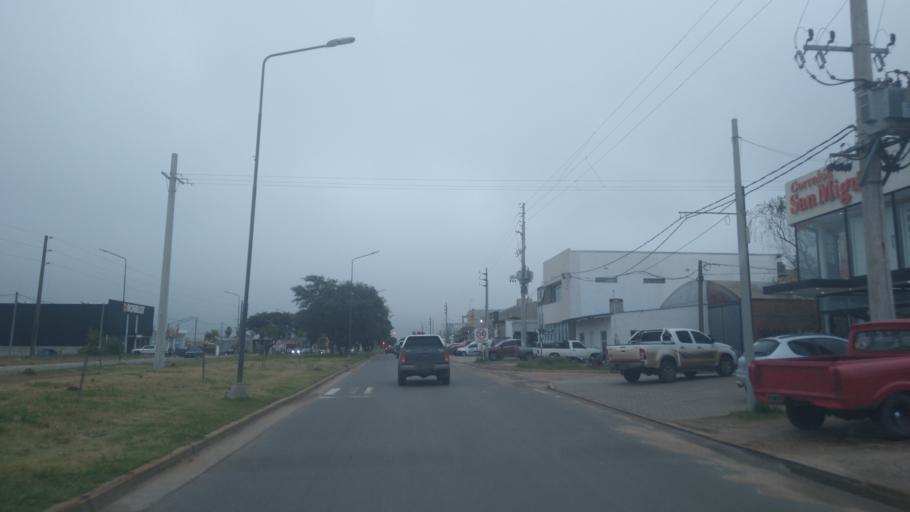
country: AR
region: Entre Rios
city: Chajari
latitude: -30.7610
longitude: -58.0040
